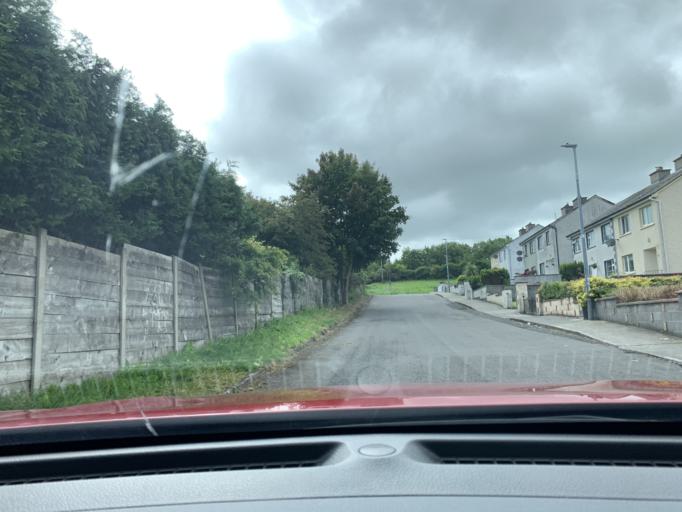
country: IE
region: Connaught
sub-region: Roscommon
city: Boyle
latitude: 53.9703
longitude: -8.2950
